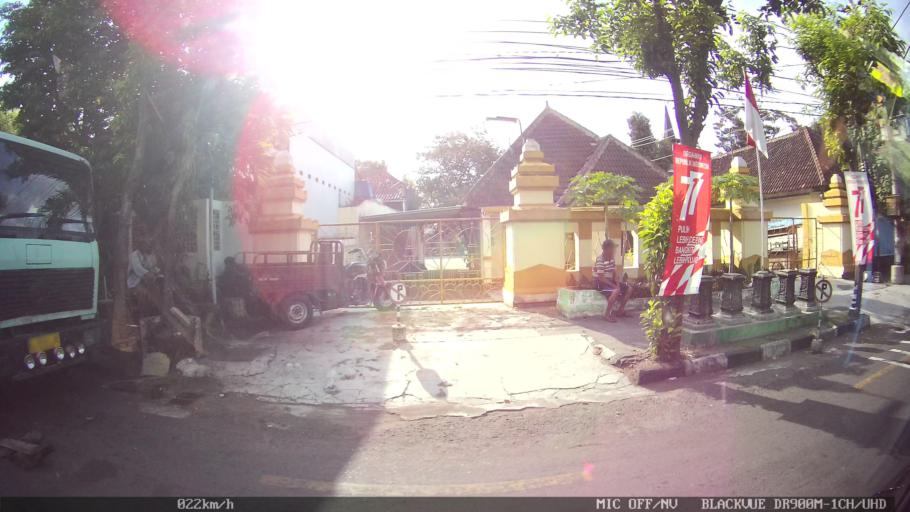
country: ID
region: Daerah Istimewa Yogyakarta
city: Kasihan
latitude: -7.8157
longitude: 110.3562
